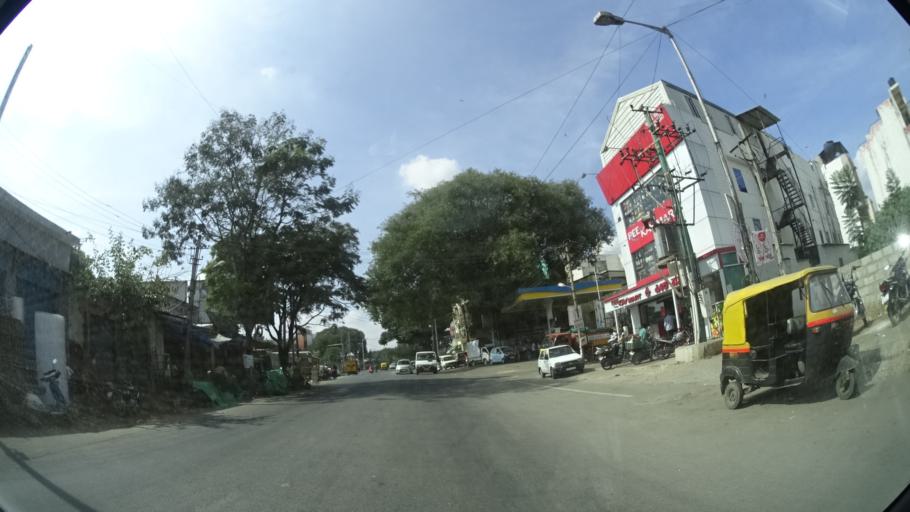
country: IN
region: Karnataka
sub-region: Bangalore Urban
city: Bangalore
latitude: 13.0050
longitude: 77.5939
